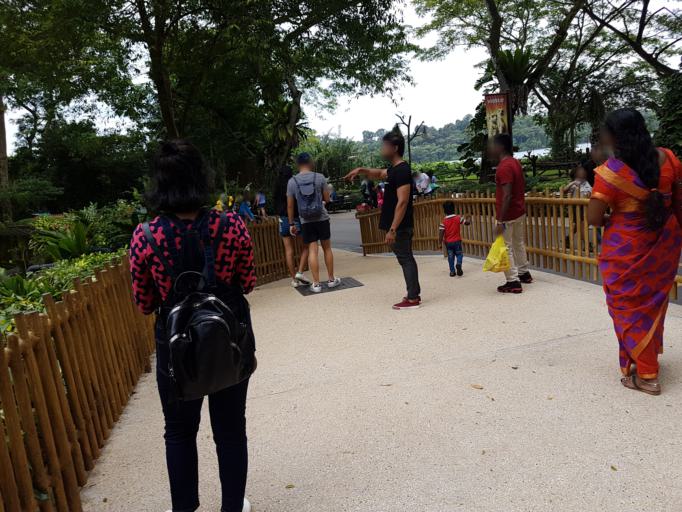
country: MY
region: Johor
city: Johor Bahru
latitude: 1.4016
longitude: 103.7941
